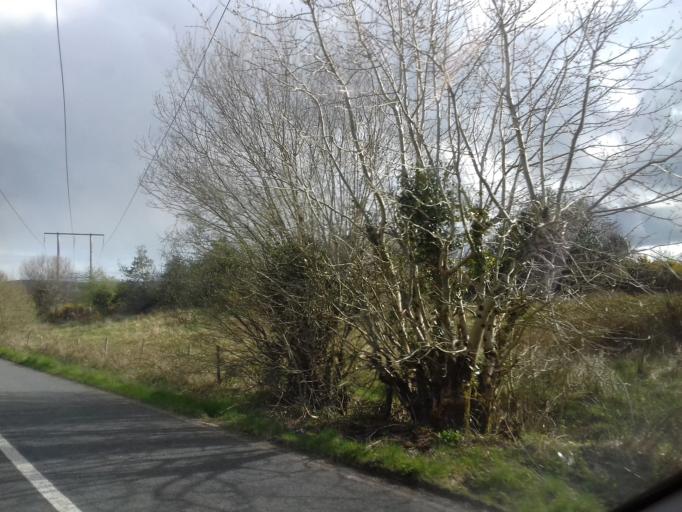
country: IE
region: Connaught
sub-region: County Leitrim
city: Manorhamilton
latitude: 54.3141
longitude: -8.1890
